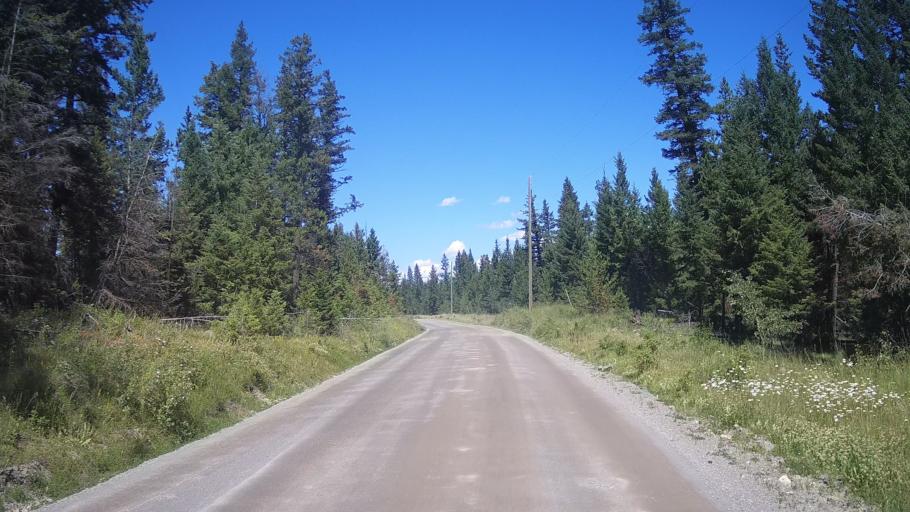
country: CA
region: British Columbia
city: Cache Creek
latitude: 51.1962
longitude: -121.5905
